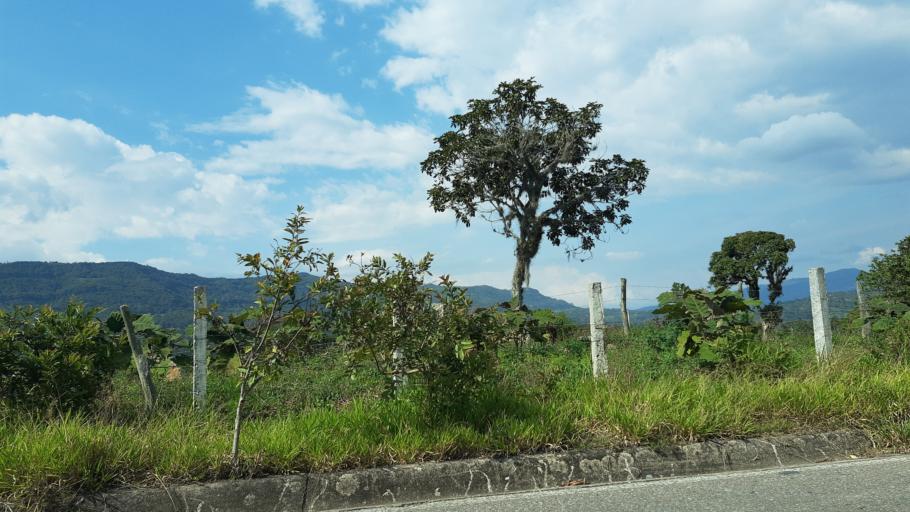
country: CO
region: Boyaca
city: Moniquira
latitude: 5.8263
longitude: -73.5942
